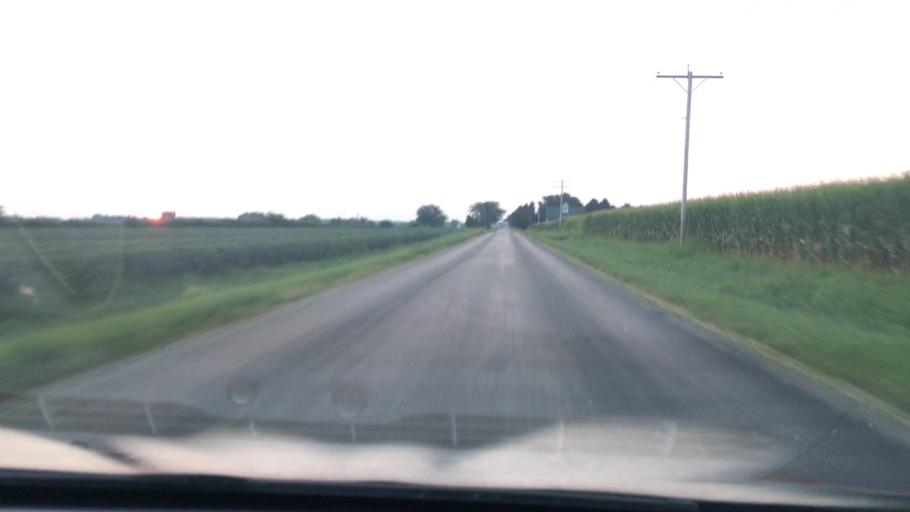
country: US
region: Illinois
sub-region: Bureau County
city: Ladd
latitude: 41.3643
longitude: -89.2067
